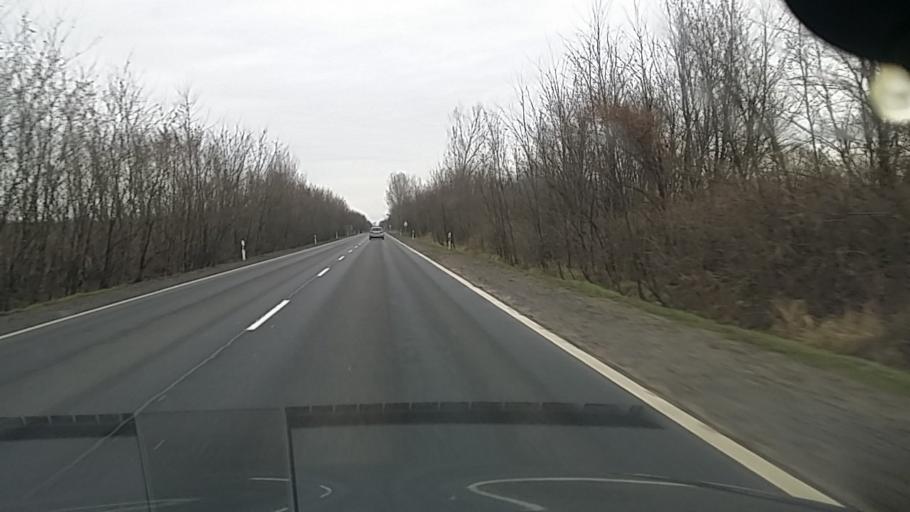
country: HU
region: Szabolcs-Szatmar-Bereg
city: Nyirbogdany
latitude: 48.0279
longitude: 21.8496
